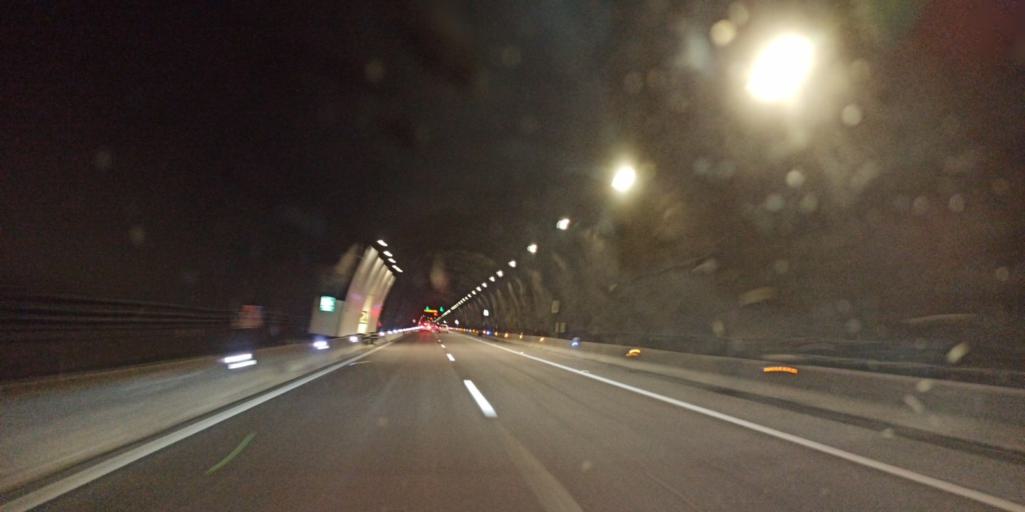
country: ES
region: Catalonia
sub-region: Provincia de Barcelona
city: Sitges
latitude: 41.2498
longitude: 1.8761
